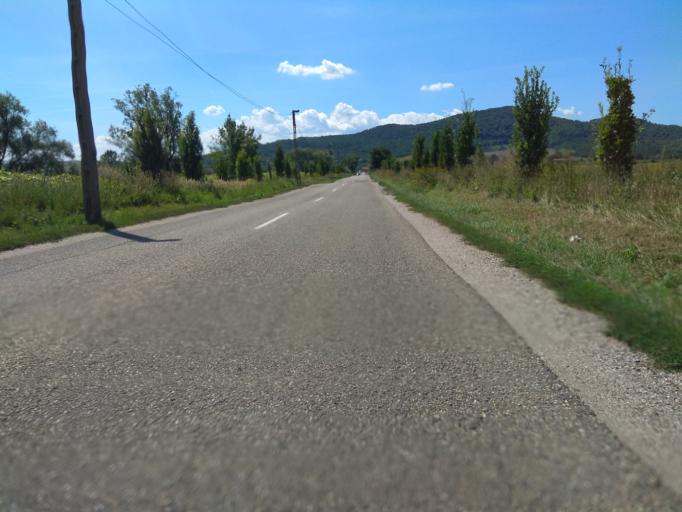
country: HU
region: Borsod-Abauj-Zemplen
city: Sajokaza
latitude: 48.2772
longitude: 20.5806
